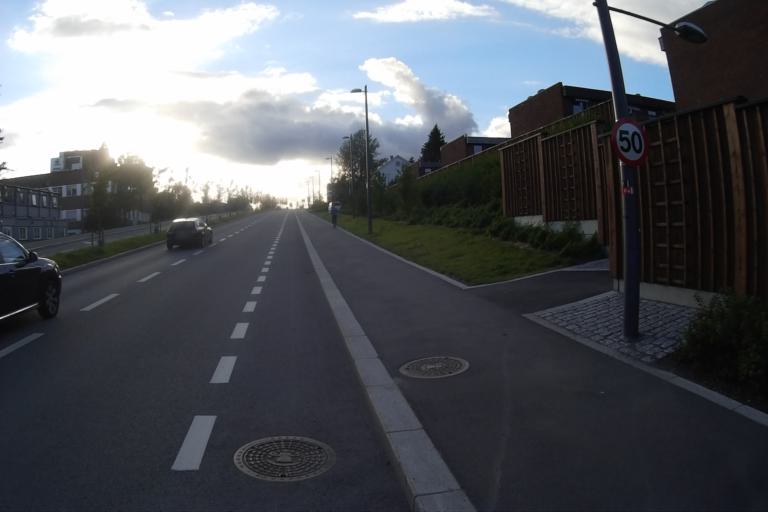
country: NO
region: Oslo
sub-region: Oslo
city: Oslo
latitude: 59.9335
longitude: 10.7957
